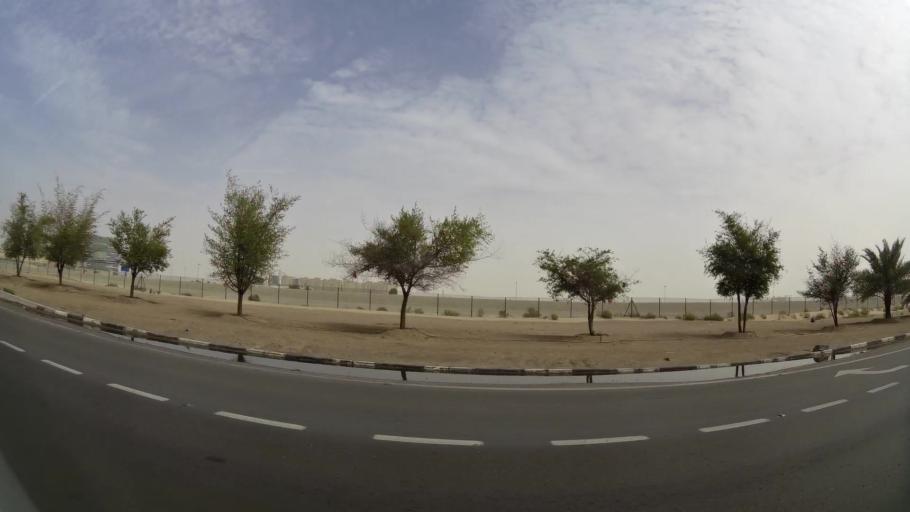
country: AE
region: Abu Dhabi
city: Abu Dhabi
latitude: 24.3680
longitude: 54.5254
